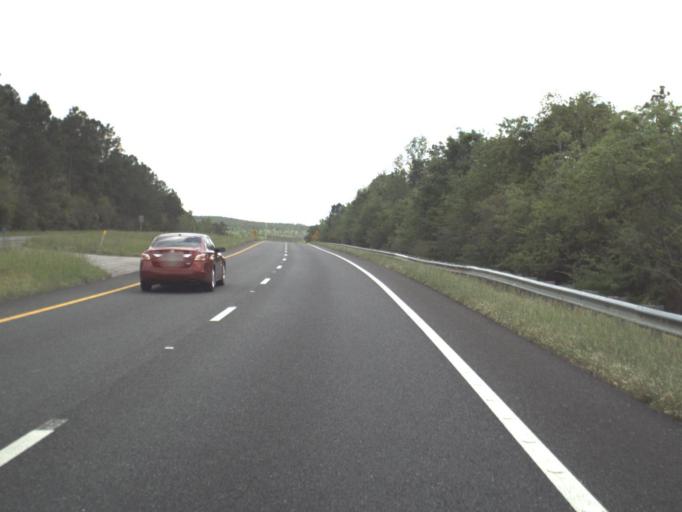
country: US
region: Florida
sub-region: Escambia County
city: Molino
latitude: 30.8028
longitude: -87.3363
